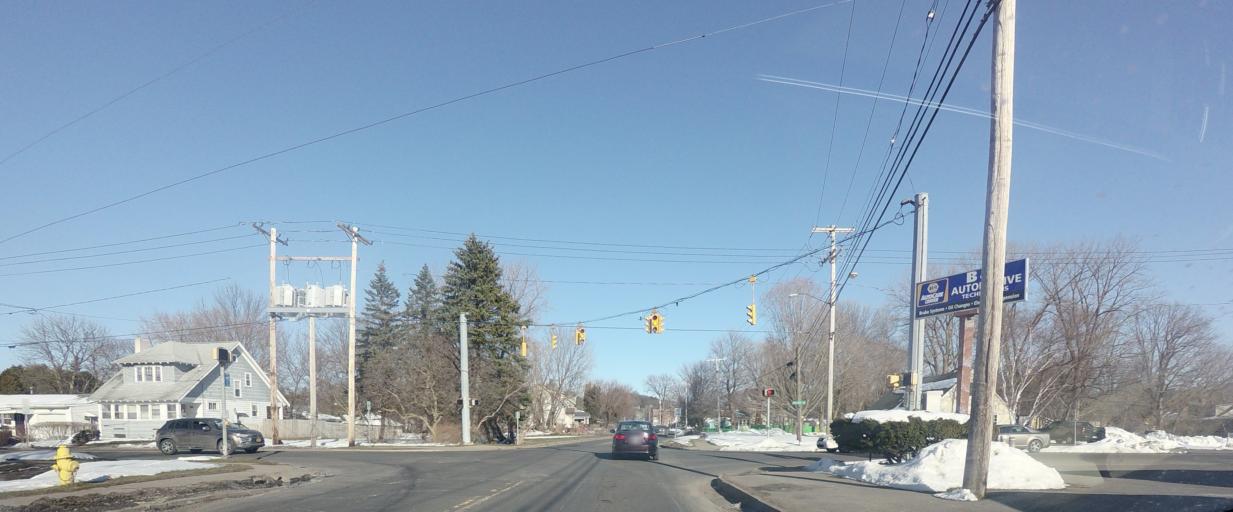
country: US
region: New York
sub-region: Onondaga County
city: Nedrow
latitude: 43.0105
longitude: -76.1479
